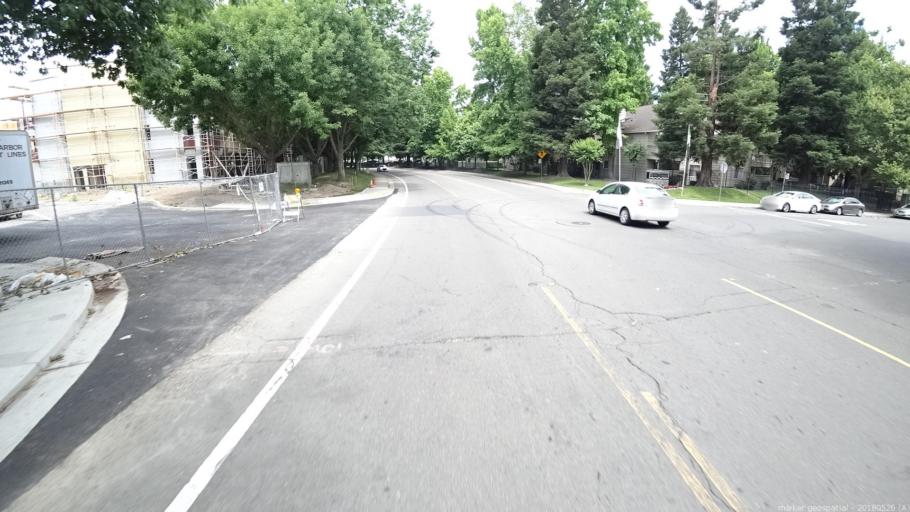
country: US
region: California
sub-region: Sacramento County
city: Sacramento
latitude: 38.6091
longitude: -121.5029
